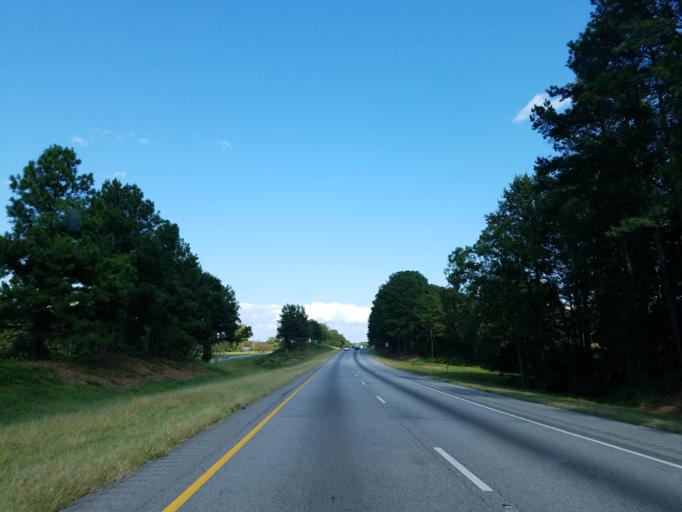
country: US
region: Georgia
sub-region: Franklin County
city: Gumlog
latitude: 34.4768
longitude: -83.0481
